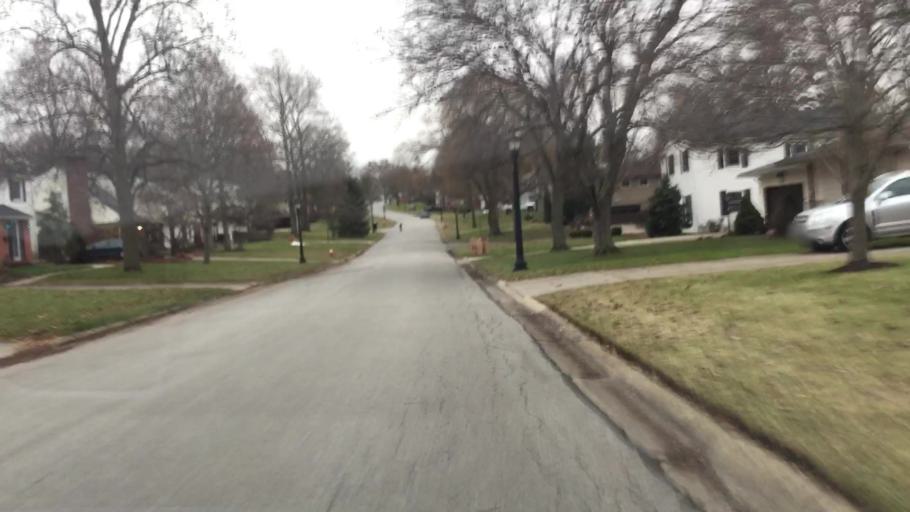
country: US
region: Ohio
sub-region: Summit County
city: Cuyahoga Falls
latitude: 41.1492
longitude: -81.5141
